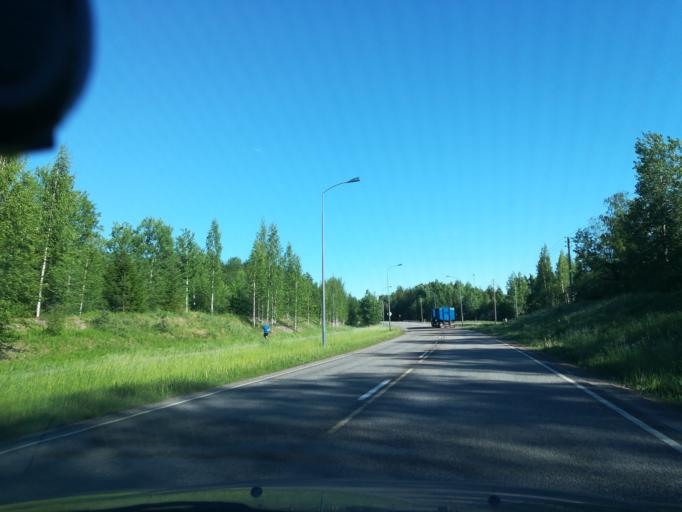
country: FI
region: South Karelia
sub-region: Imatra
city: Imatra
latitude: 61.1589
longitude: 28.7919
